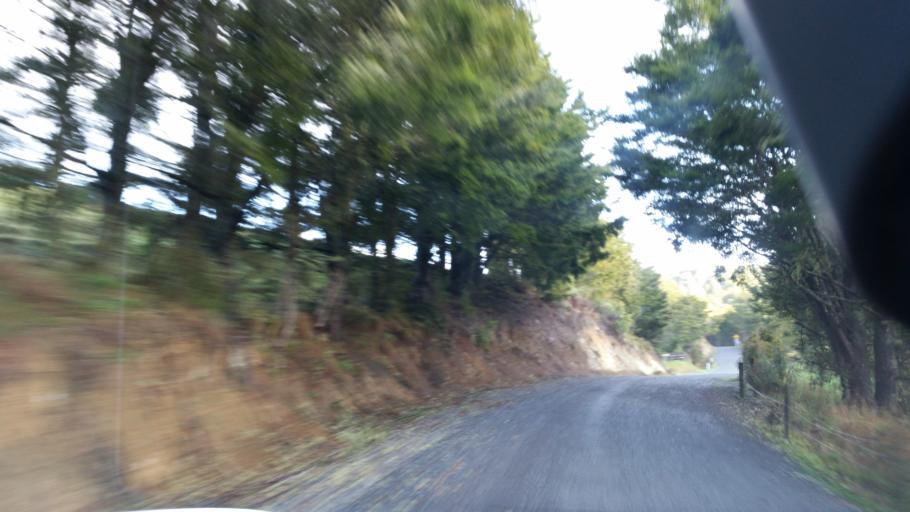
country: NZ
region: Northland
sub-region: Whangarei
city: Maungatapere
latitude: -35.7794
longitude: 174.0918
